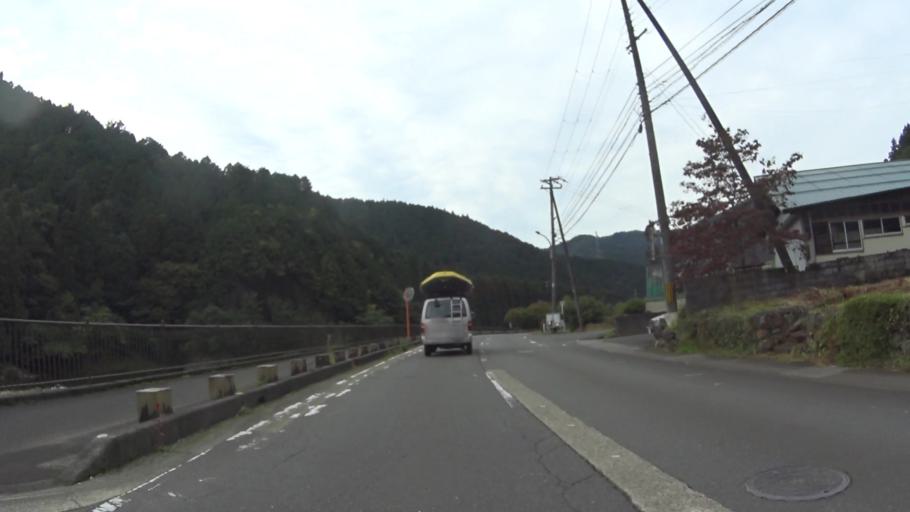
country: JP
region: Fukui
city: Obama
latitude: 35.3105
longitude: 135.6353
